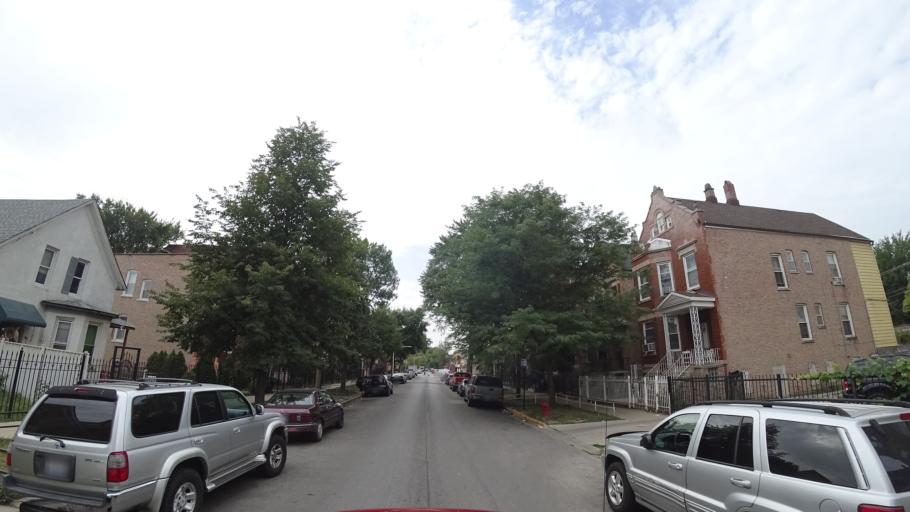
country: US
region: Illinois
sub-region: Cook County
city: Cicero
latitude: 41.8456
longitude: -87.7112
